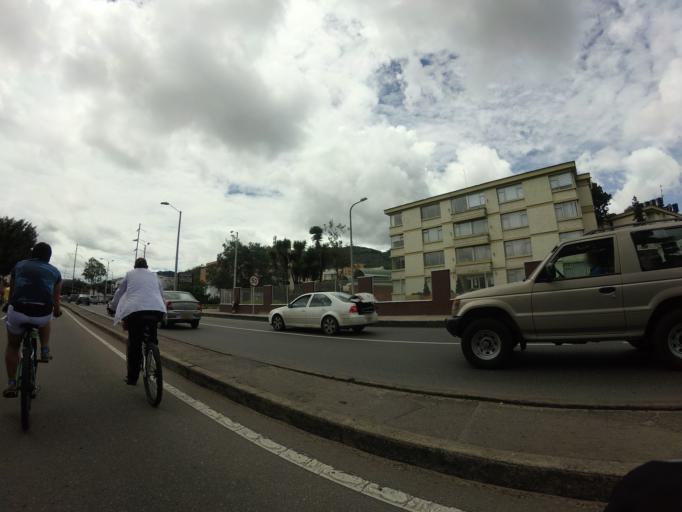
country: CO
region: Bogota D.C.
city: Barrio San Luis
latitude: 4.6865
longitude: -74.0351
